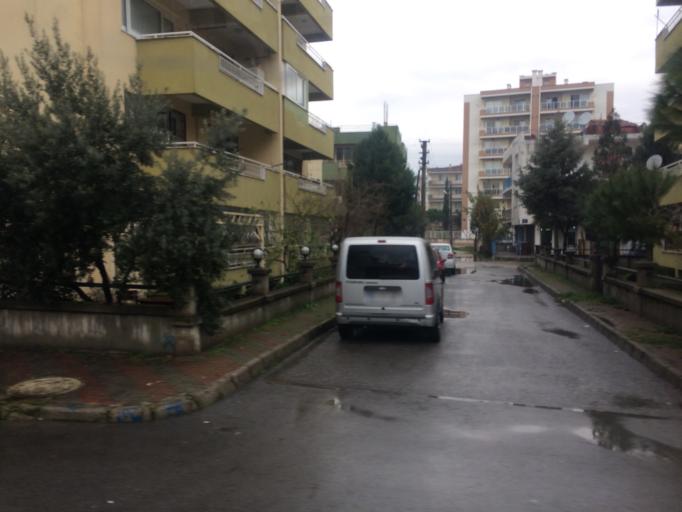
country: TR
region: Izmir
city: Karsiyaka
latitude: 38.4909
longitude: 27.0563
